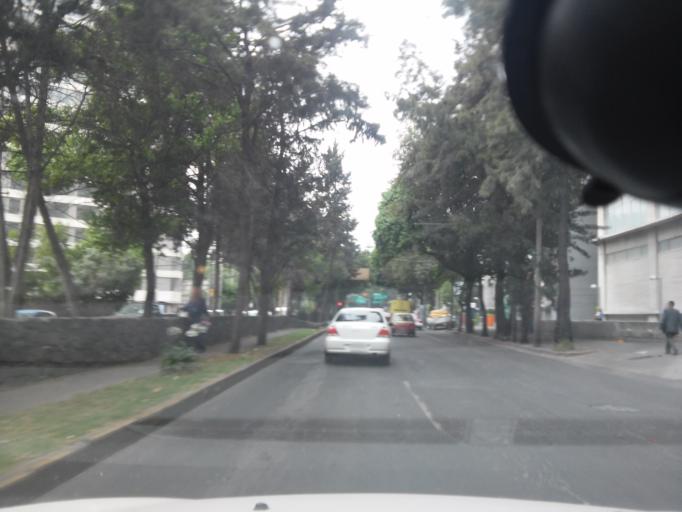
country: MX
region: Mexico City
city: Miguel Hidalgo
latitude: 19.4410
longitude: -99.1835
